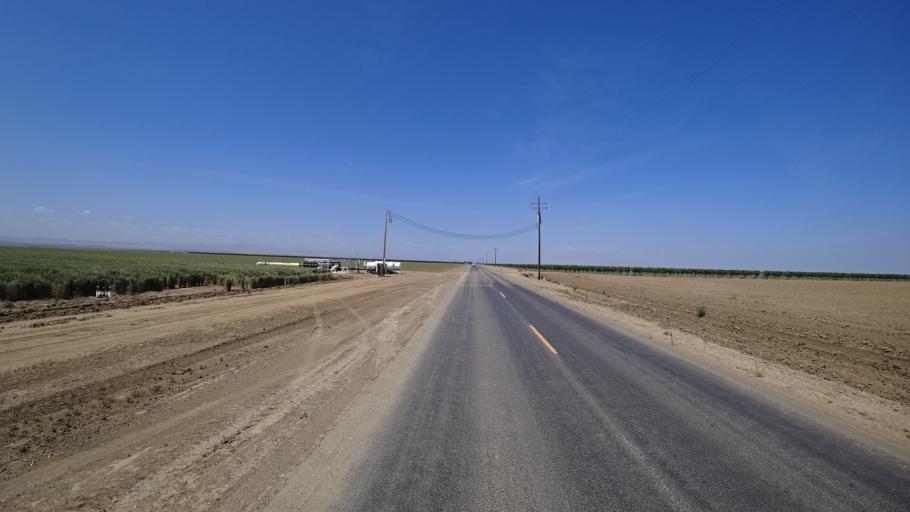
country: US
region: California
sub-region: Kings County
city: Kettleman City
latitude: 36.1377
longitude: -119.9494
